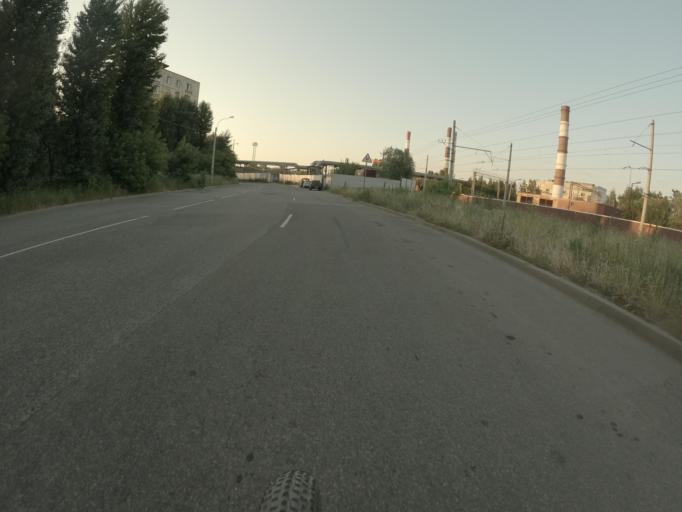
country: RU
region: St.-Petersburg
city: Avtovo
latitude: 59.8668
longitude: 30.2799
